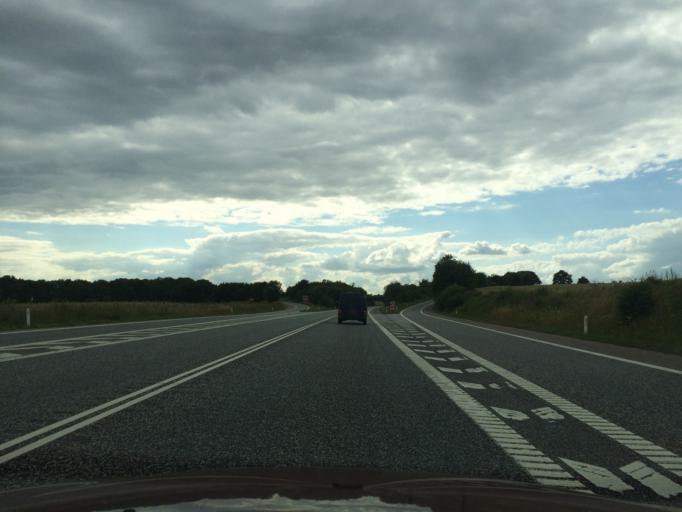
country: DK
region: Central Jutland
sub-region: Syddjurs Kommune
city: Ronde
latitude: 56.3156
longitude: 10.4350
